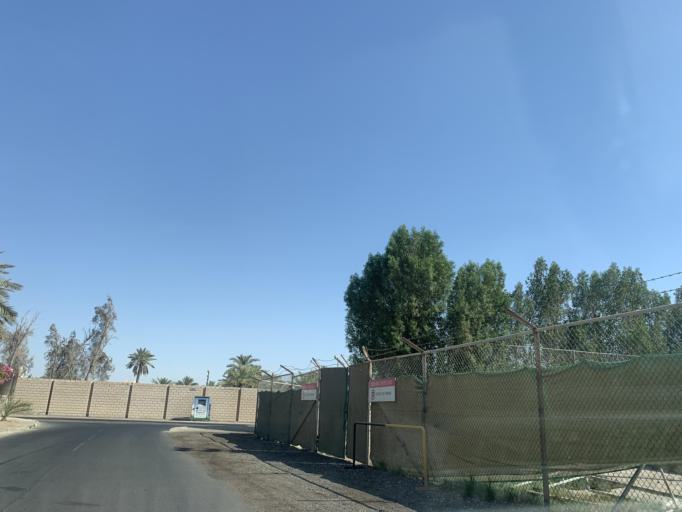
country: BH
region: Northern
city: Madinat `Isa
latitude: 26.1925
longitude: 50.4723
